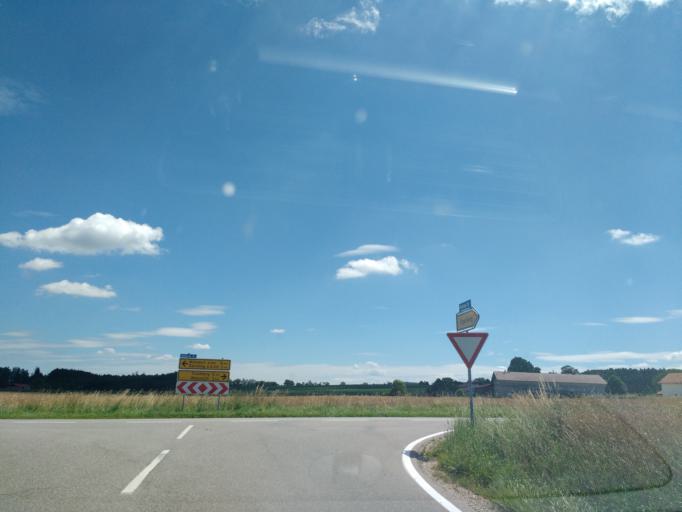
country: DE
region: Bavaria
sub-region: Upper Bavaria
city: Engelsberg
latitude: 48.1211
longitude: 12.5489
